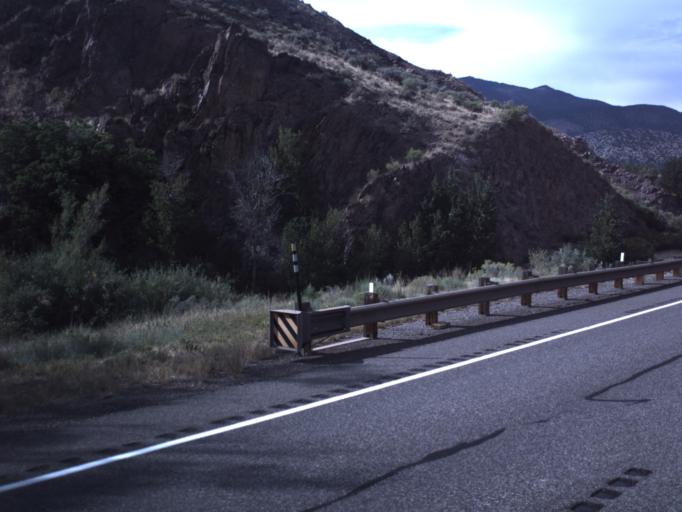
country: US
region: Utah
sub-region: Sevier County
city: Monroe
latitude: 38.5795
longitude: -112.2579
